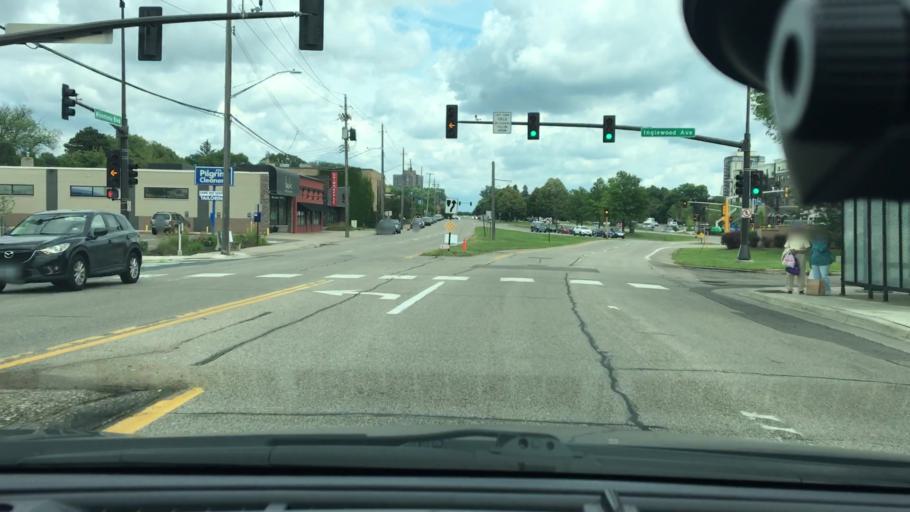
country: US
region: Minnesota
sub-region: Hennepin County
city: Saint Louis Park
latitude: 44.9485
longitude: -93.3331
